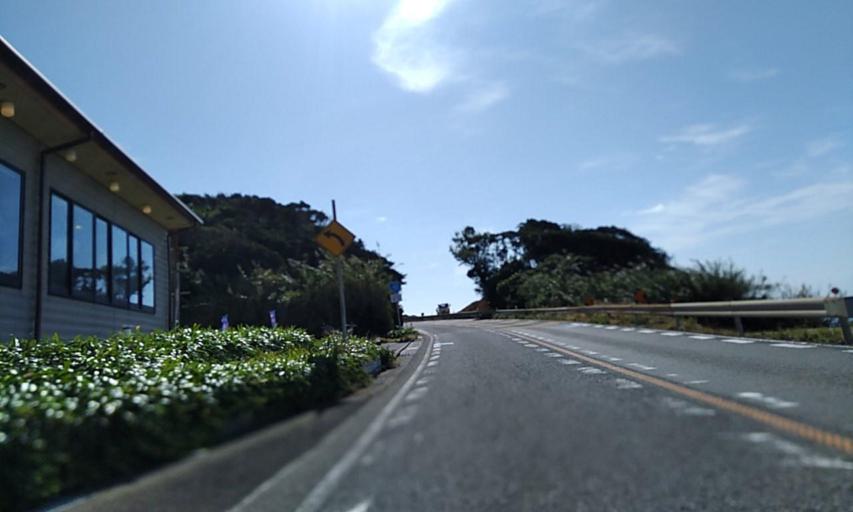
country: JP
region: Wakayama
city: Gobo
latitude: 33.7856
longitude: 135.2342
